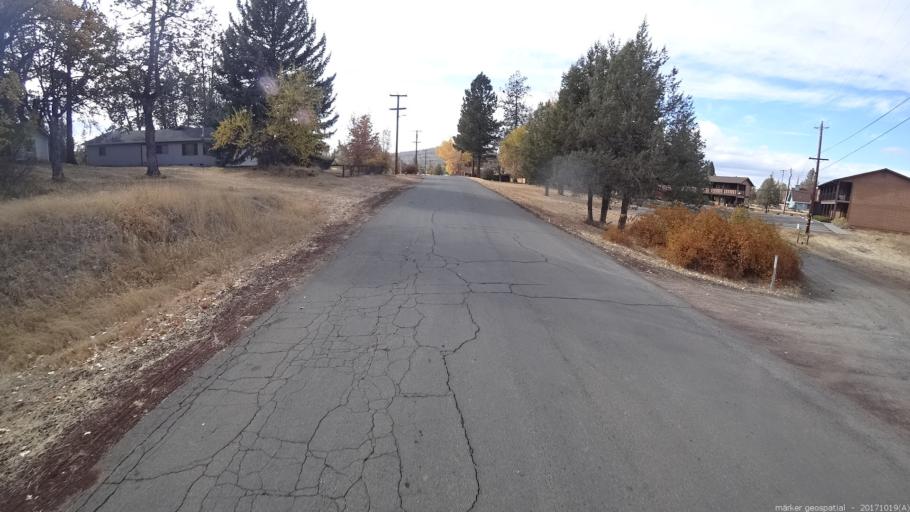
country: US
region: California
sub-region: Shasta County
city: Burney
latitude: 41.0010
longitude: -121.4441
